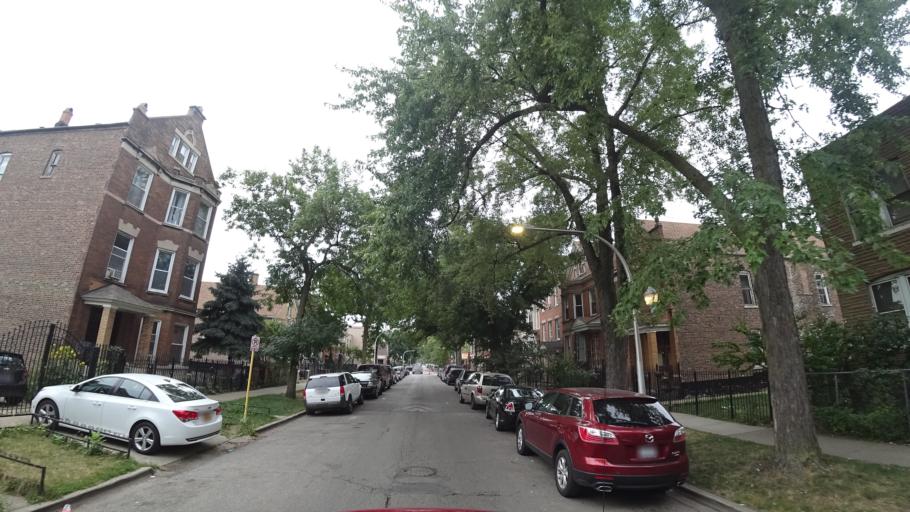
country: US
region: Illinois
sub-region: Cook County
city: Cicero
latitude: 41.8471
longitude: -87.7112
